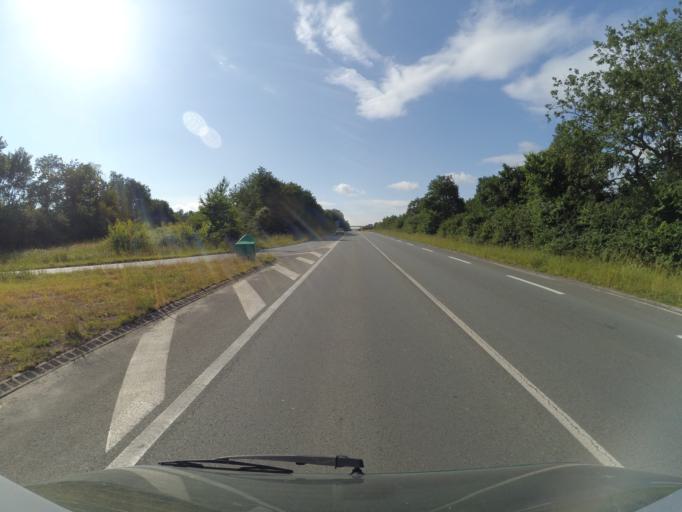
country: FR
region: Poitou-Charentes
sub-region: Departement de la Charente-Maritime
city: Saint-Agnant
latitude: 45.8384
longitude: -0.9438
